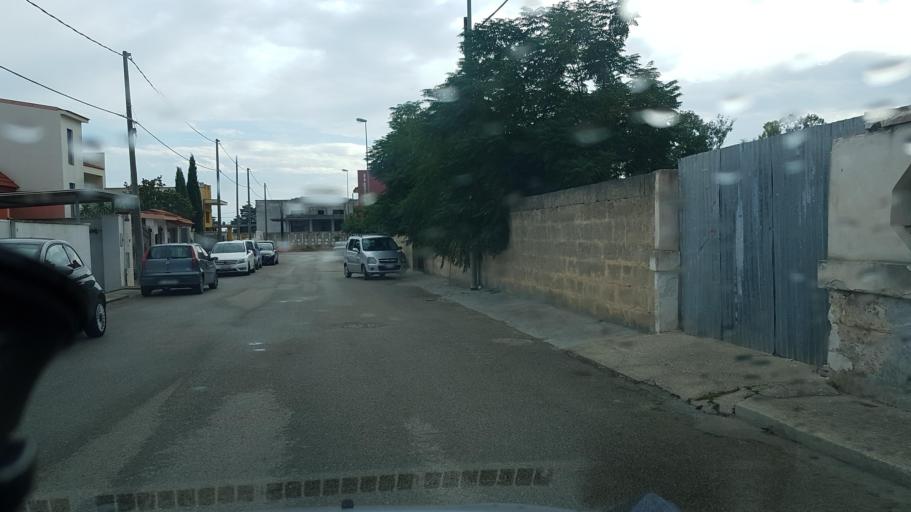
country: IT
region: Apulia
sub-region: Provincia di Brindisi
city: Torre Santa Susanna
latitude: 40.4681
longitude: 17.7307
